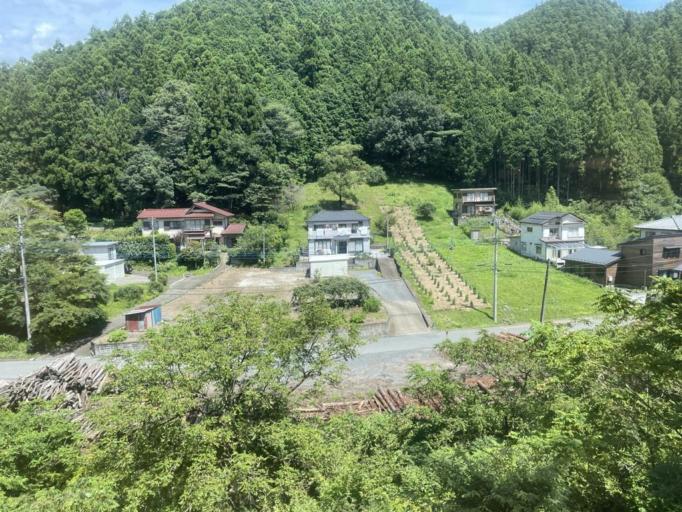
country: JP
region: Saitama
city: Morohongo
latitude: 35.9353
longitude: 139.1960
